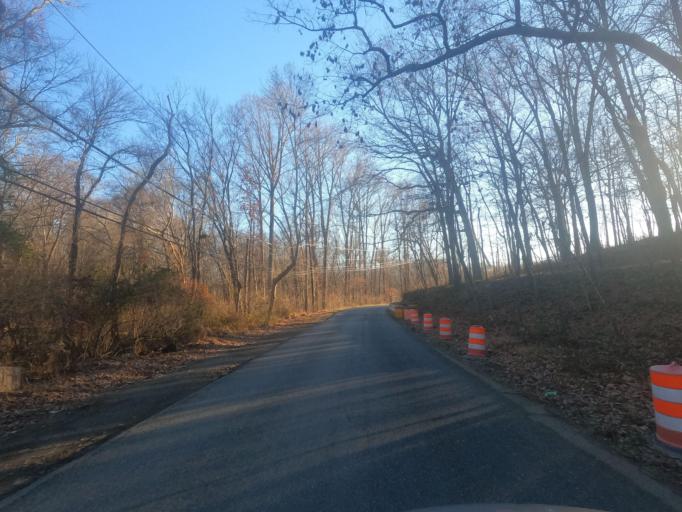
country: US
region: Maryland
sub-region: Montgomery County
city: Olney
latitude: 39.1823
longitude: -77.0654
